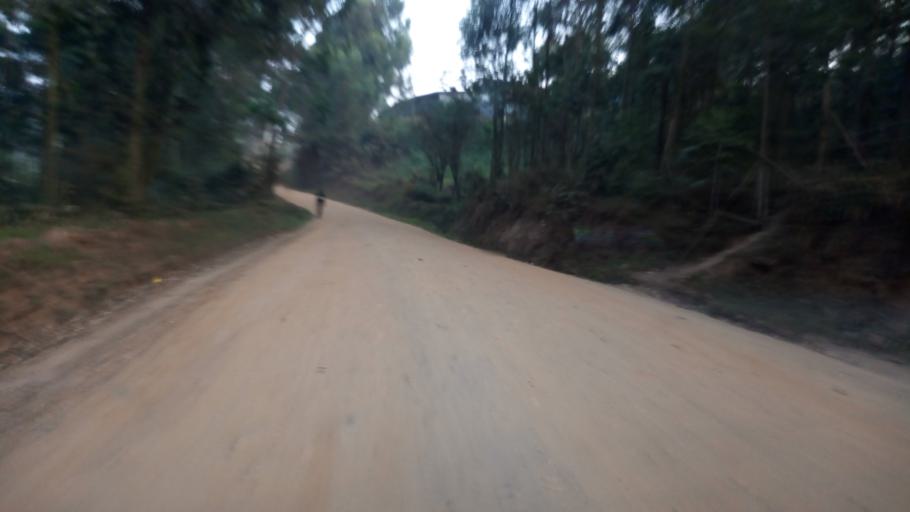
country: UG
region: Western Region
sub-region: Rukungiri District
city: Rukungiri
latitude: -0.7760
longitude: 29.9245
